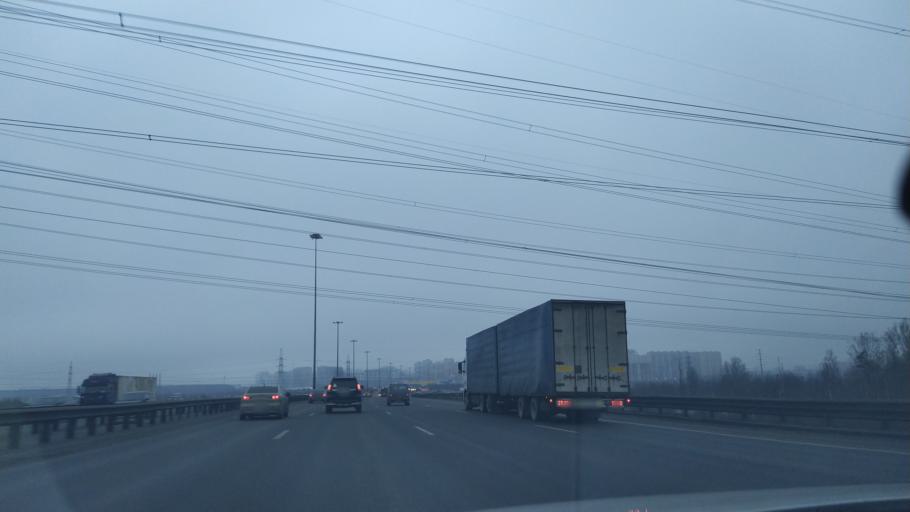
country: RU
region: St.-Petersburg
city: Krasnogvargeisky
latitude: 59.9304
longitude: 30.5358
